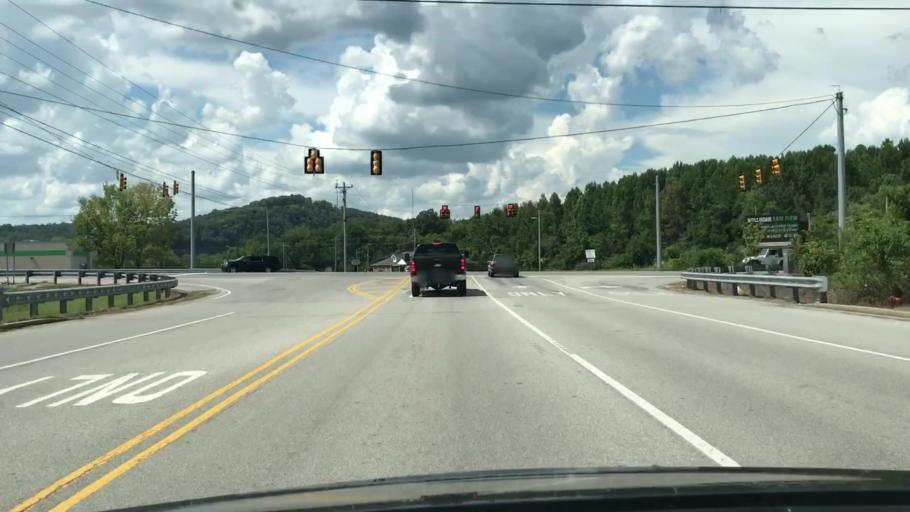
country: US
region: Tennessee
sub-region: Smith County
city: South Carthage
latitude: 36.2441
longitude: -85.9415
